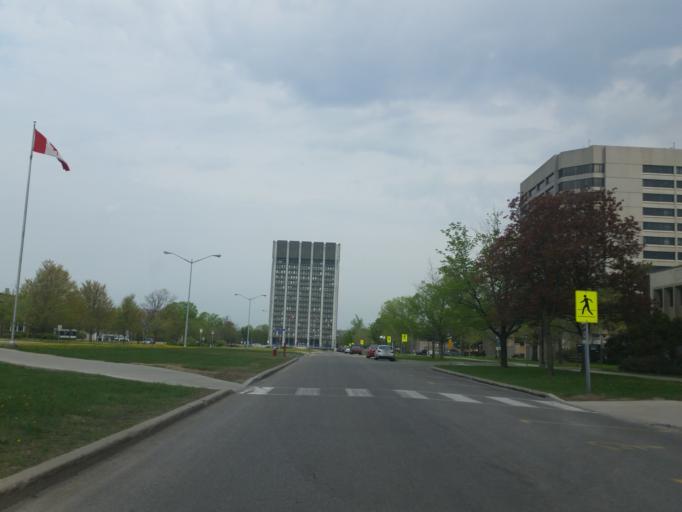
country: CA
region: Ontario
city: Ottawa
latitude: 45.4048
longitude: -75.7347
